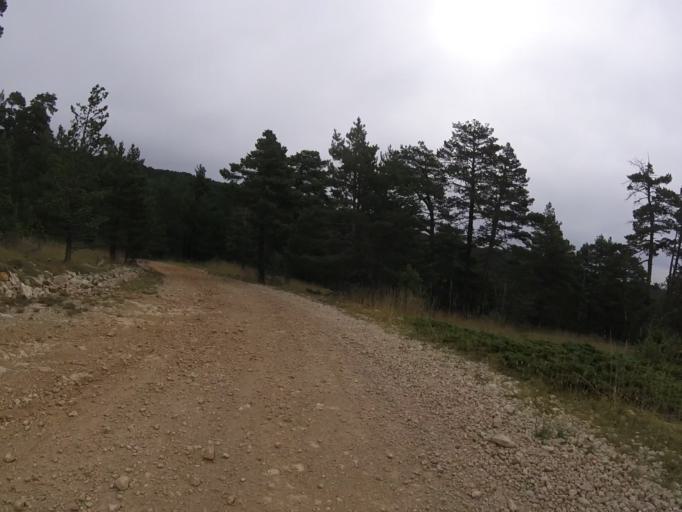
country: ES
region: Aragon
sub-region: Provincia de Teruel
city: Valdelinares
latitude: 40.3603
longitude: -0.6122
